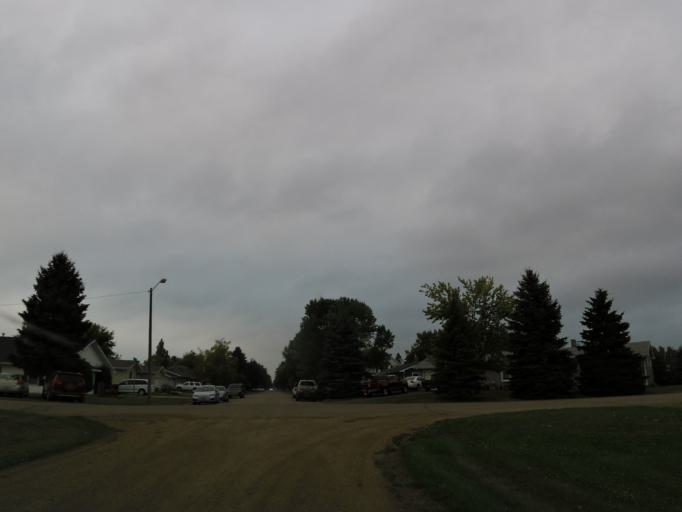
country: US
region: North Dakota
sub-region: Walsh County
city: Grafton
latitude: 48.5567
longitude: -97.1819
